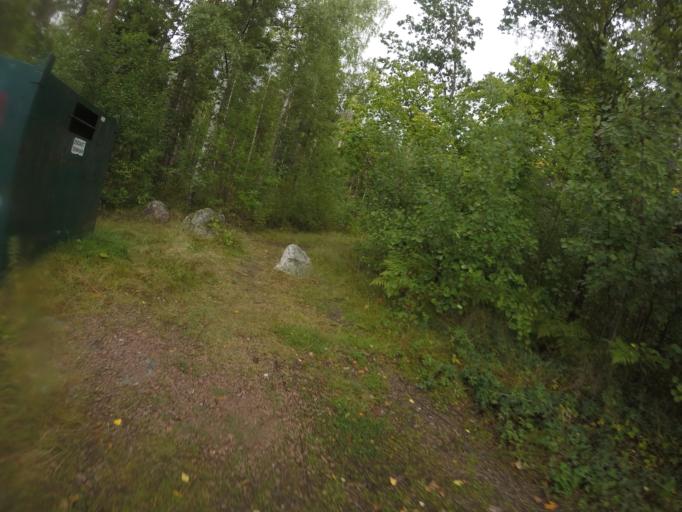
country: SE
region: Vaestmanland
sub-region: Vasteras
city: Vasteras
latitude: 59.6398
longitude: 16.5194
